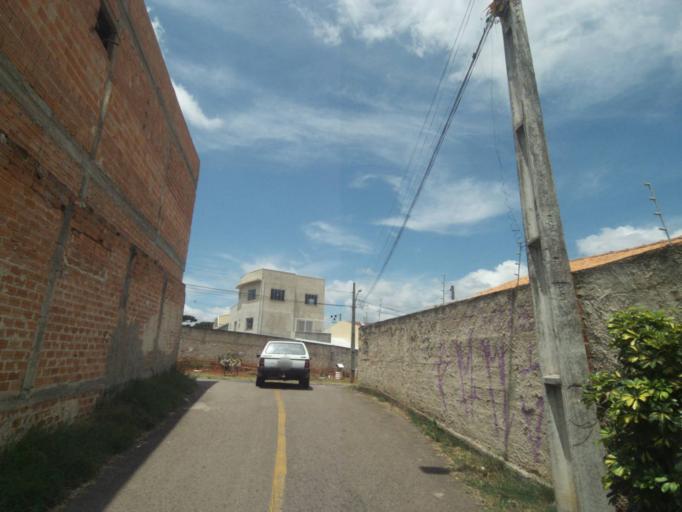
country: BR
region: Parana
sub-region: Curitiba
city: Curitiba
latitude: -25.4601
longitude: -49.3486
